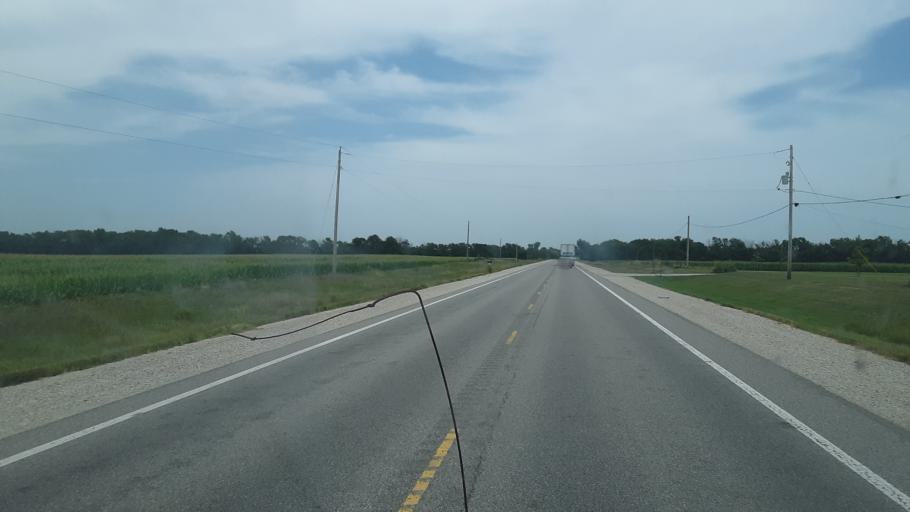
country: US
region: Kansas
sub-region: Allen County
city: Iola
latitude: 37.9217
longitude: -95.2035
